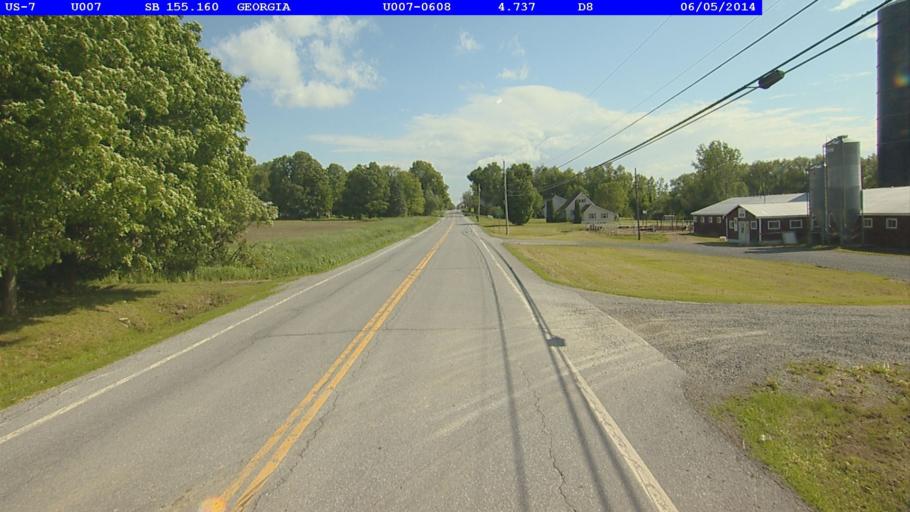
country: US
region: Vermont
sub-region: Franklin County
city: Saint Albans
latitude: 44.7395
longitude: -73.1150
